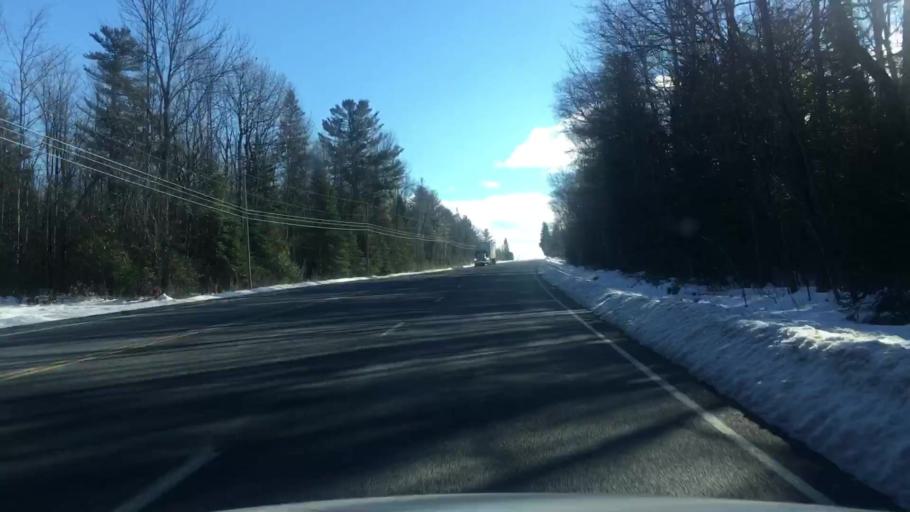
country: US
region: Maine
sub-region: Somerset County
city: Madison
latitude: 44.8983
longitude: -69.8102
